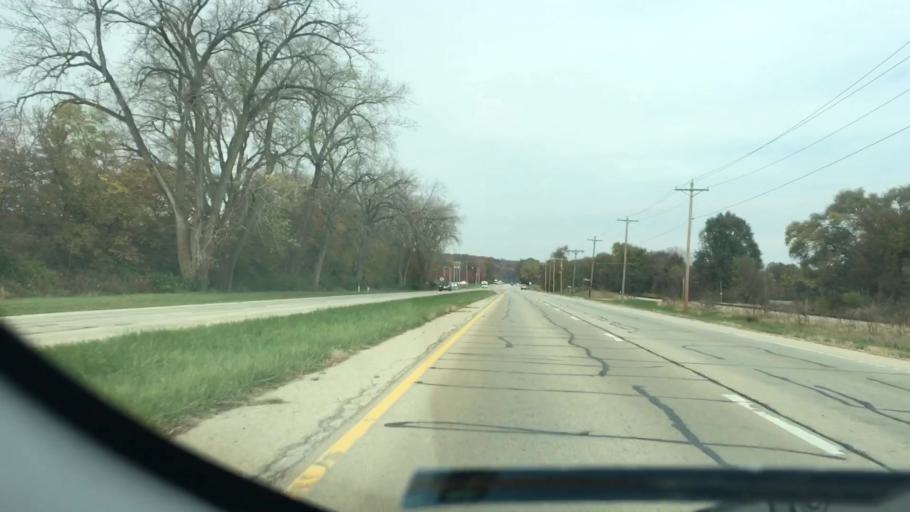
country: US
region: Illinois
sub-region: Peoria County
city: Peoria Heights
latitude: 40.7621
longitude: -89.5672
